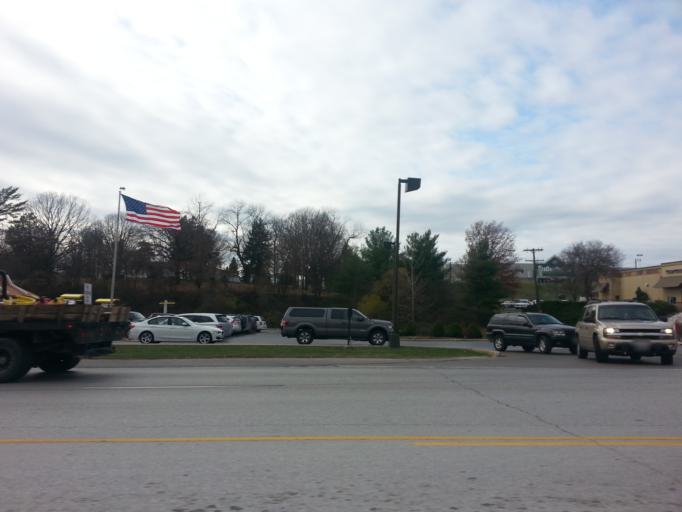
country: US
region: Missouri
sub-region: Marion County
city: Hannibal
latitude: 39.7207
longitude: -91.3920
